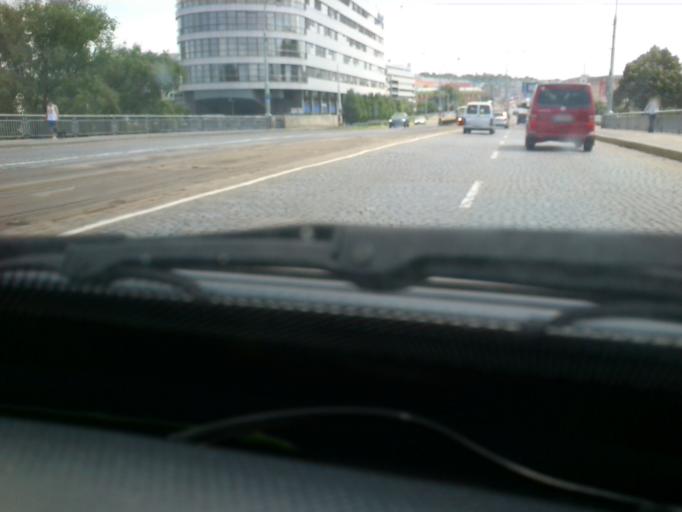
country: CZ
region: Praha
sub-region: Praha 8
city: Karlin
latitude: 50.0946
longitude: 14.4369
